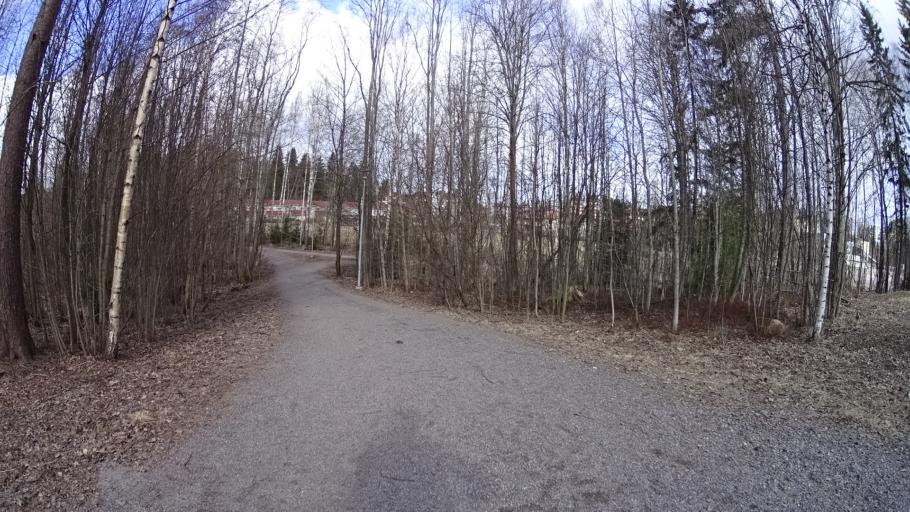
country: FI
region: Uusimaa
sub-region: Helsinki
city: Kilo
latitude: 60.2138
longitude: 24.7903
